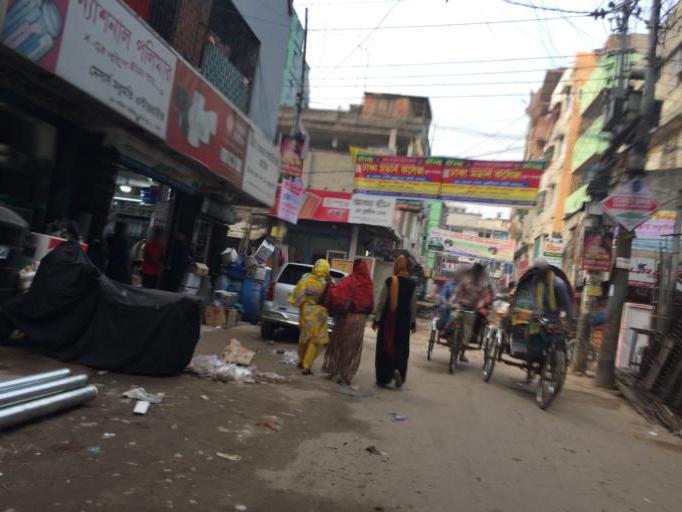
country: BD
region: Dhaka
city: Azimpur
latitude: 23.7965
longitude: 90.3526
